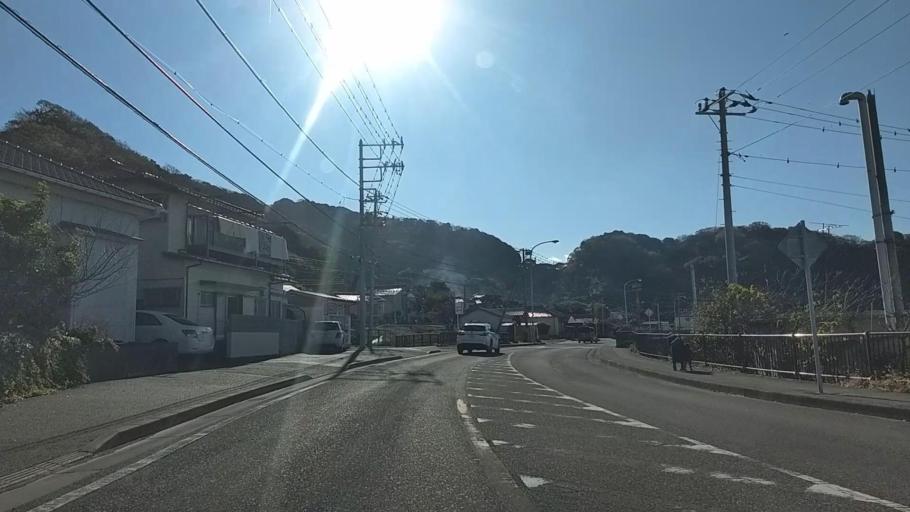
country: JP
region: Chiba
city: Tateyama
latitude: 35.1316
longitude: 139.8397
